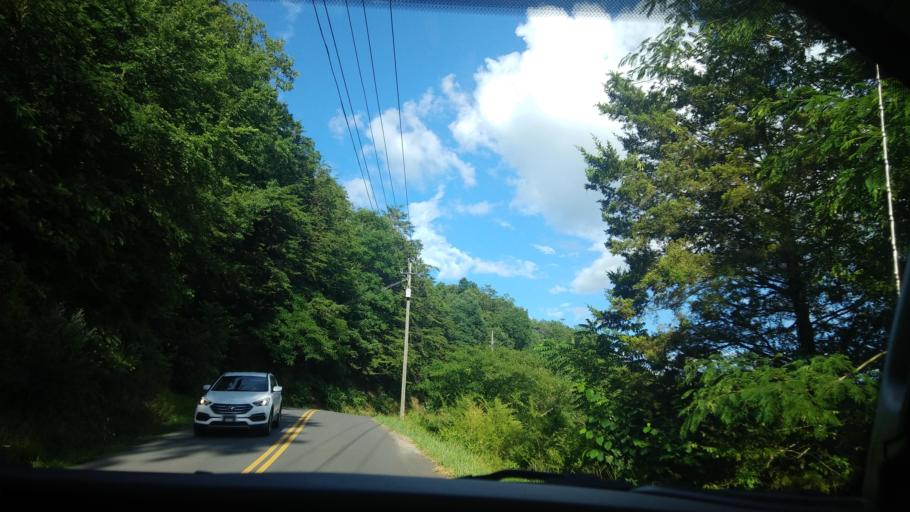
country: US
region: Tennessee
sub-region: Sevier County
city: Pigeon Forge
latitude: 35.7634
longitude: -83.5665
